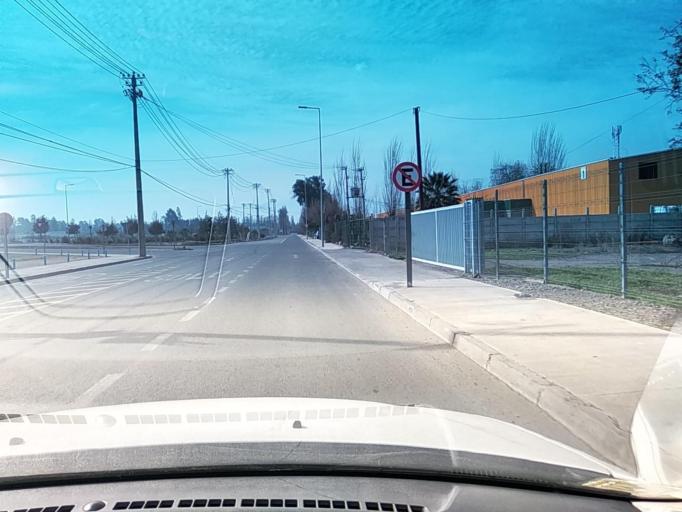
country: CL
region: Santiago Metropolitan
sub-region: Provincia de Chacabuco
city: Chicureo Abajo
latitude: -33.2877
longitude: -70.7336
